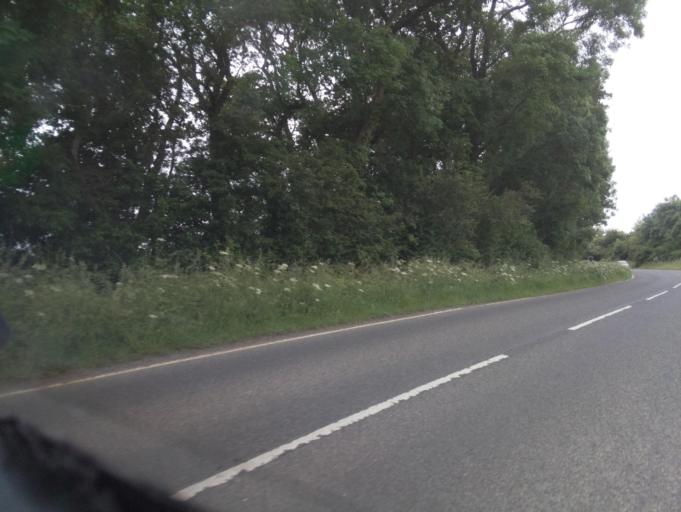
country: GB
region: England
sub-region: District of Rutland
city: Wing
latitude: 52.6362
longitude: -0.6687
